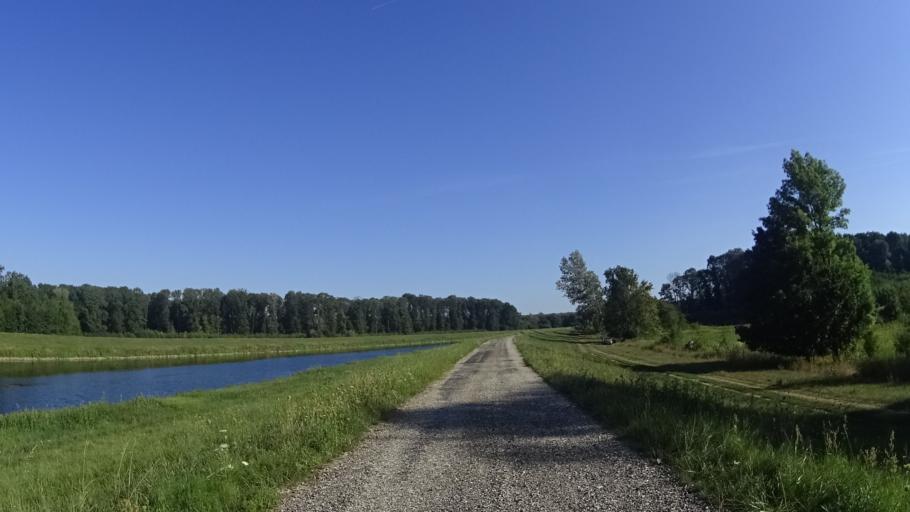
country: CZ
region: South Moravian
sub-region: Okres Breclav
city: Lanzhot
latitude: 48.7051
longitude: 16.9975
